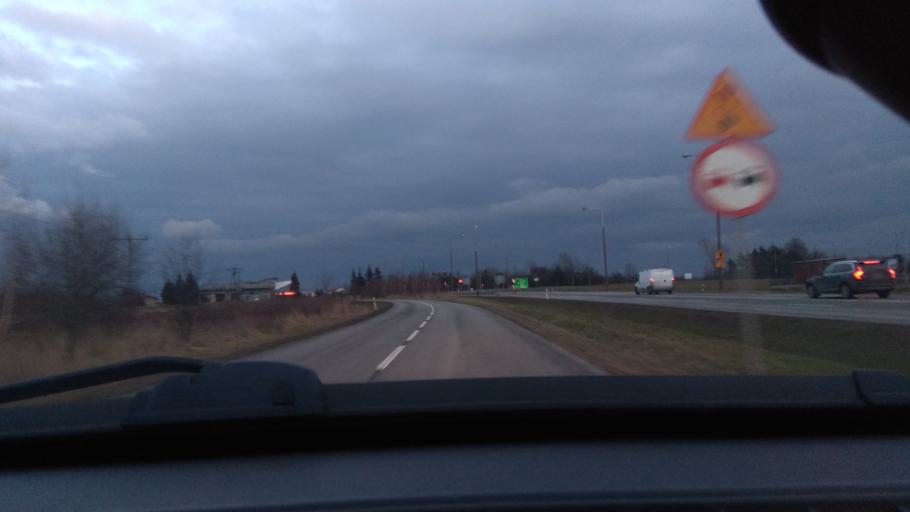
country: PL
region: Greater Poland Voivodeship
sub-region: Powiat kepinski
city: Kepno
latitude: 51.2881
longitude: 18.0114
